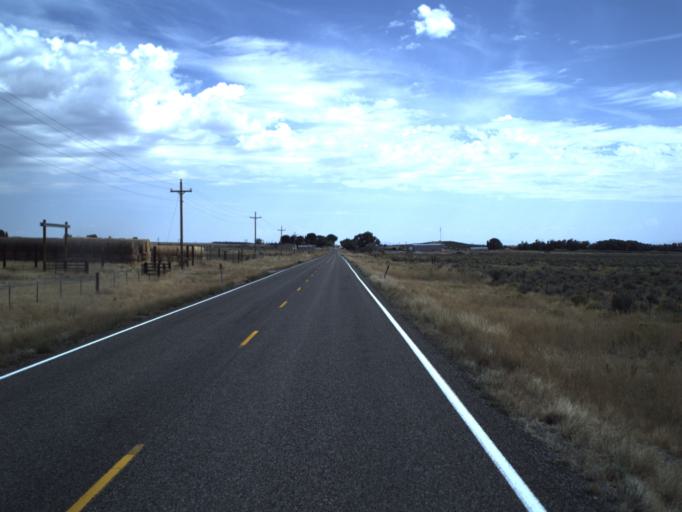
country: US
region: Idaho
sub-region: Cassia County
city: Burley
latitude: 41.8168
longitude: -113.3436
